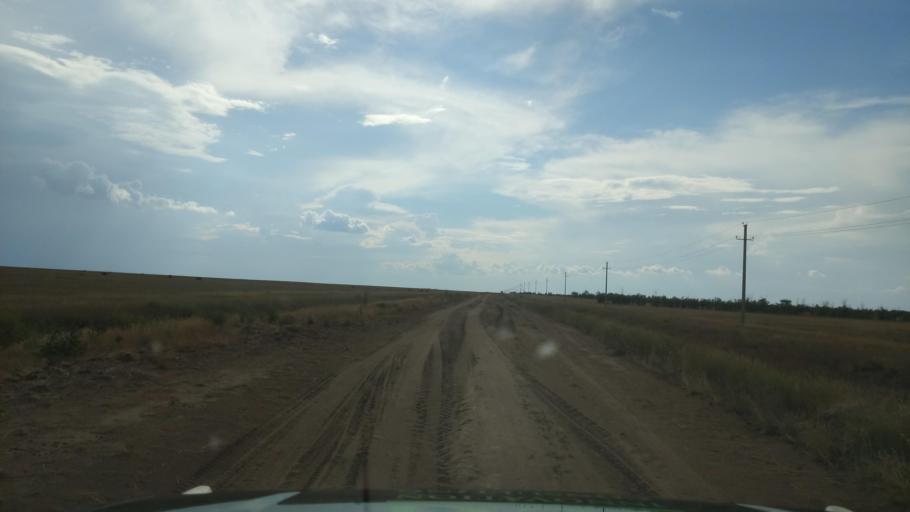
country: KZ
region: Pavlodar
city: Pavlodar
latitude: 52.5125
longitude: 77.5088
